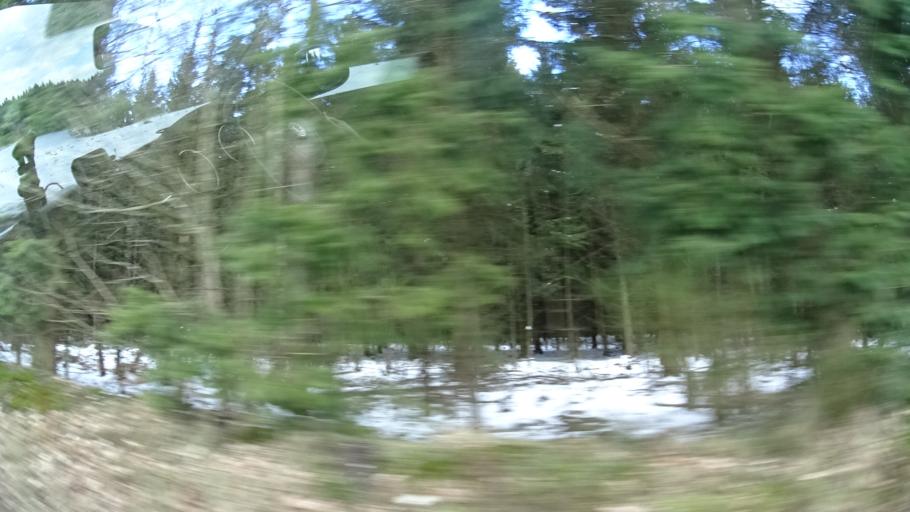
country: DE
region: Thuringia
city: Benshausen
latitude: 50.6234
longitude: 10.6265
